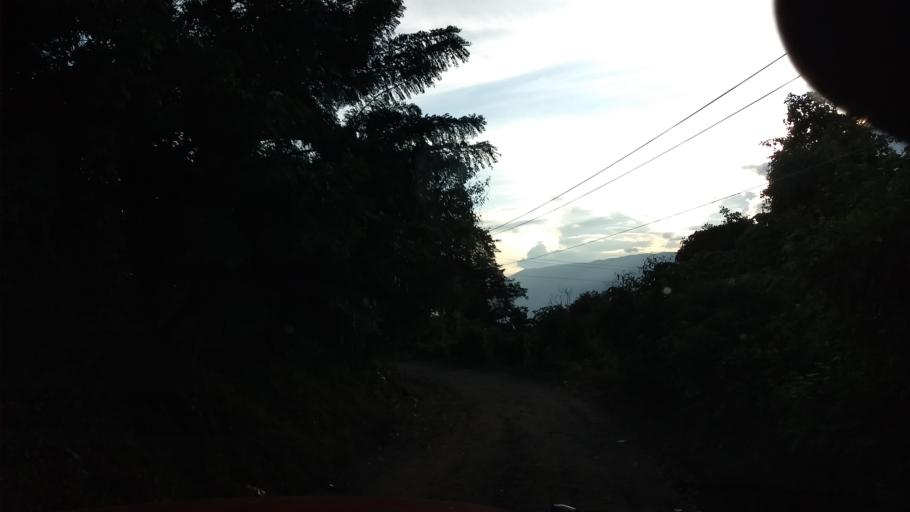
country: MX
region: Jalisco
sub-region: San Gabriel
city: Alista
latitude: 19.5101
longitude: -103.7519
